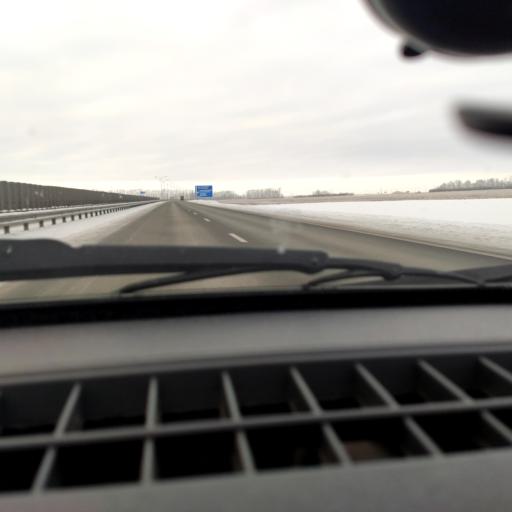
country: RU
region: Bashkortostan
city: Kushnarenkovo
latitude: 55.0657
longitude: 55.3354
